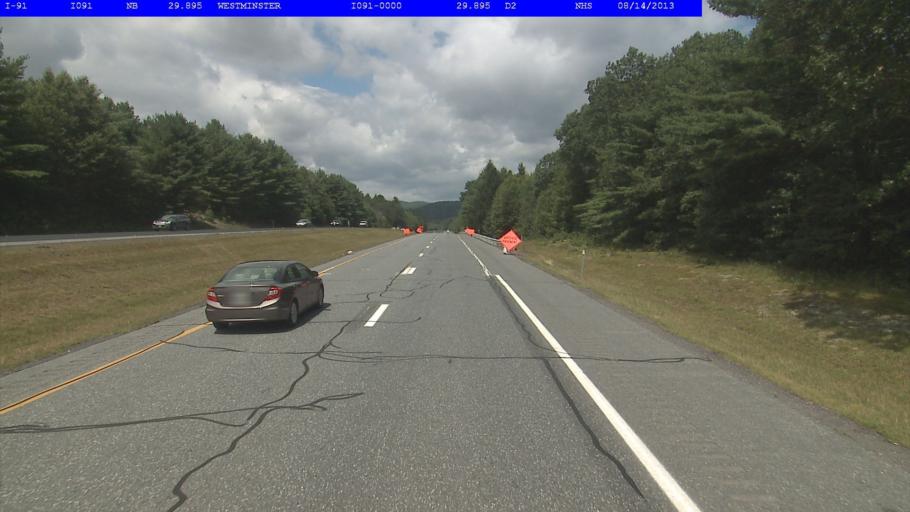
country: US
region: Vermont
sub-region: Windham County
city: Bellows Falls
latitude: 43.1090
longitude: -72.4561
